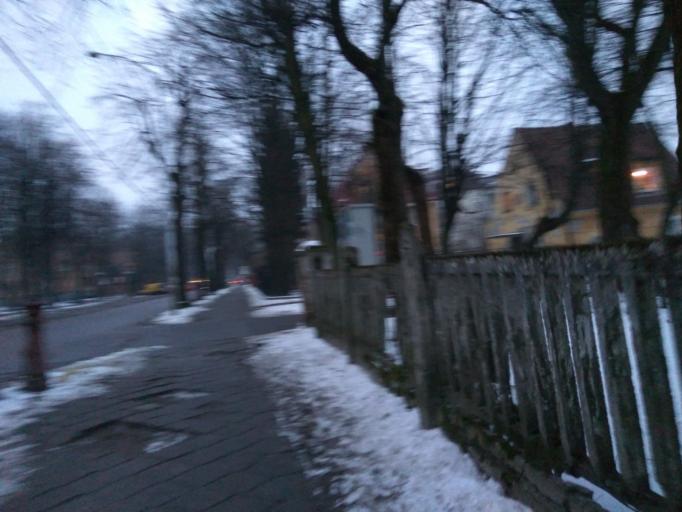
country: RU
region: Kaliningrad
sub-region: Gorod Kaliningrad
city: Kaliningrad
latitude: 54.7179
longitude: 20.4714
